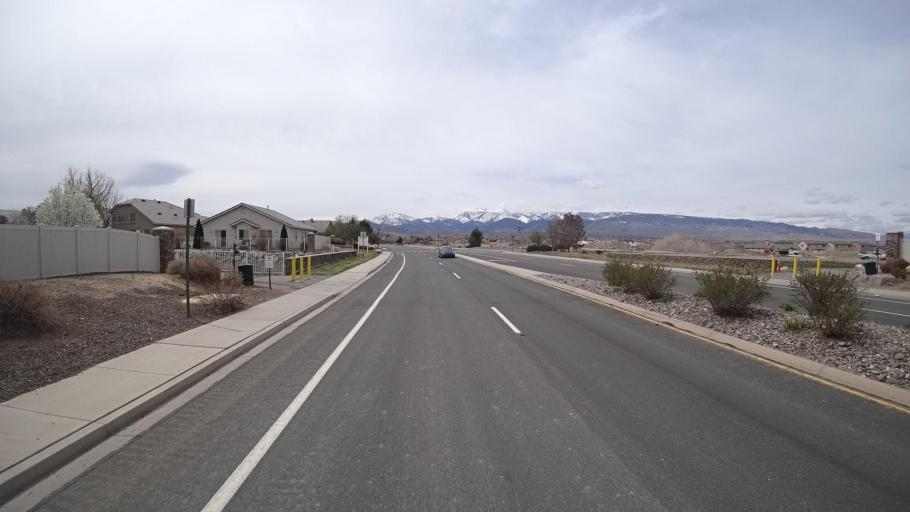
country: US
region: Nevada
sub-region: Washoe County
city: Sparks
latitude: 39.4171
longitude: -119.7227
